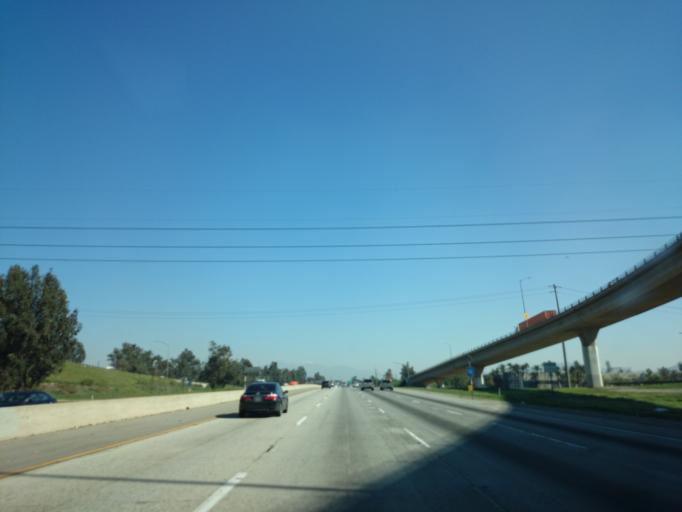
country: US
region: California
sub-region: San Bernardino County
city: Rancho Cucamonga
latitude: 34.0673
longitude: -117.5437
